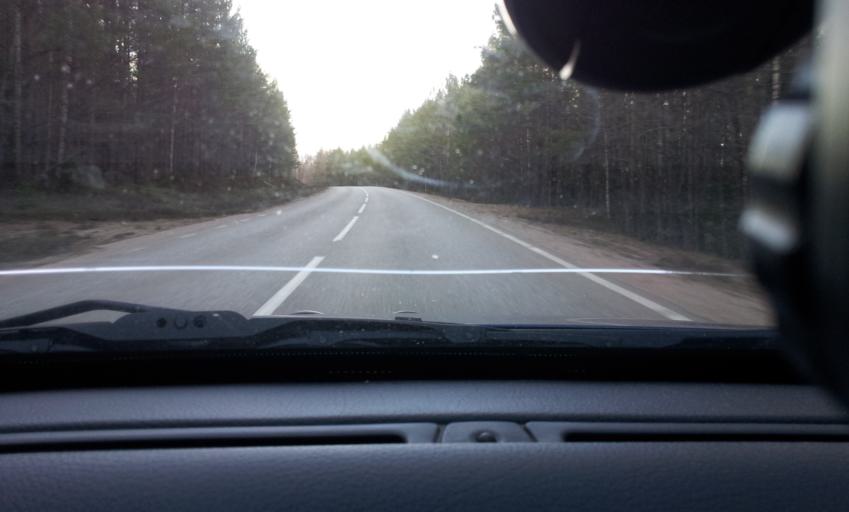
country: SE
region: Vaesternorrland
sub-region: Ange Kommun
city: Ange
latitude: 62.0895
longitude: 15.0928
